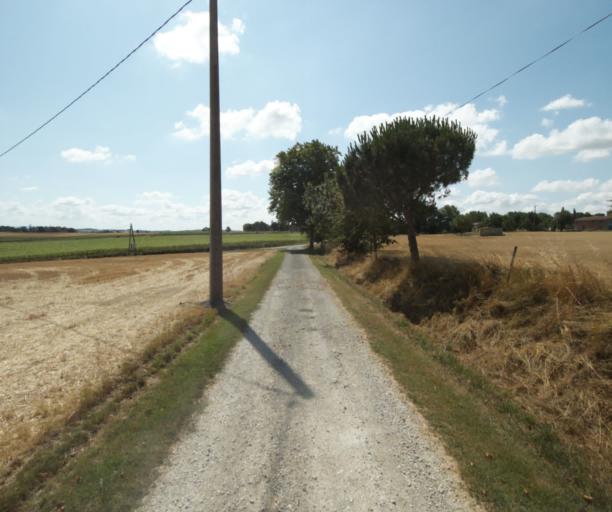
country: FR
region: Midi-Pyrenees
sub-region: Departement de la Haute-Garonne
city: Auriac-sur-Vendinelle
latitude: 43.4533
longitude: 1.7885
